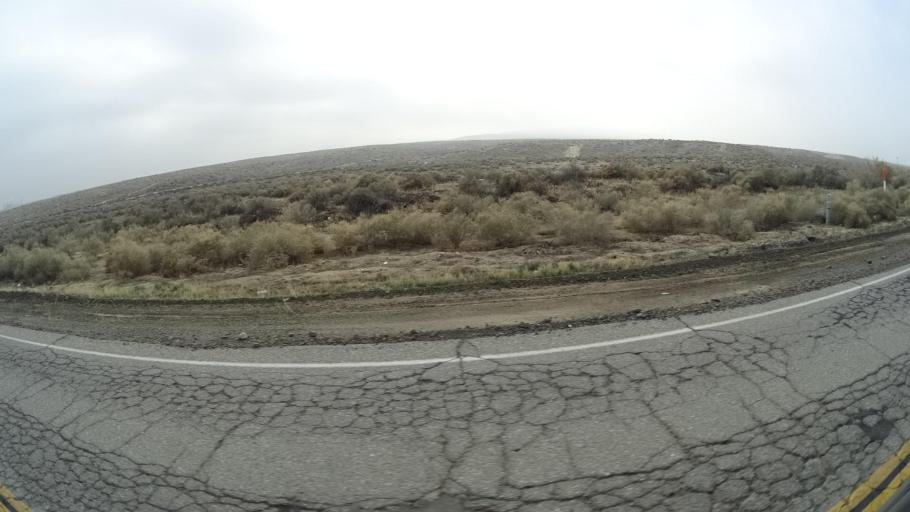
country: US
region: California
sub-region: Kern County
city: South Taft
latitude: 35.1341
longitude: -119.4061
